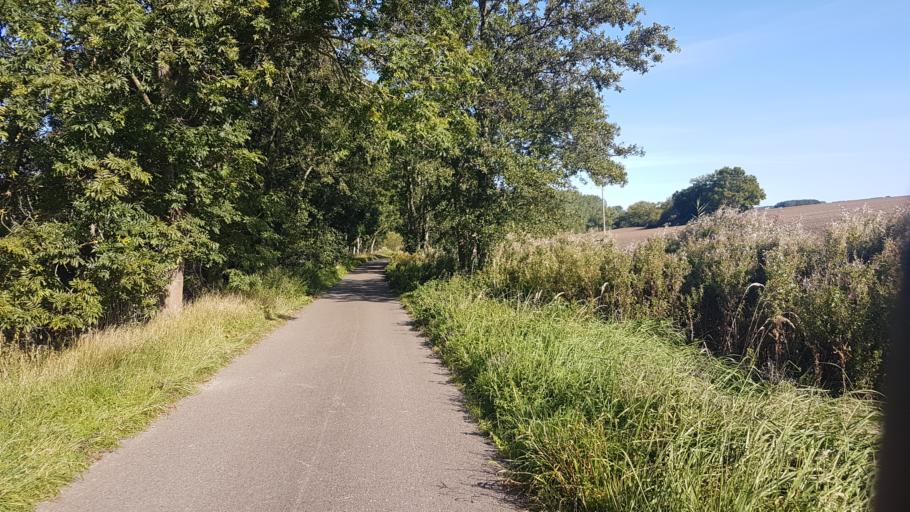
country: DE
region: Mecklenburg-Vorpommern
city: Sagard
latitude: 54.5057
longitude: 13.5220
